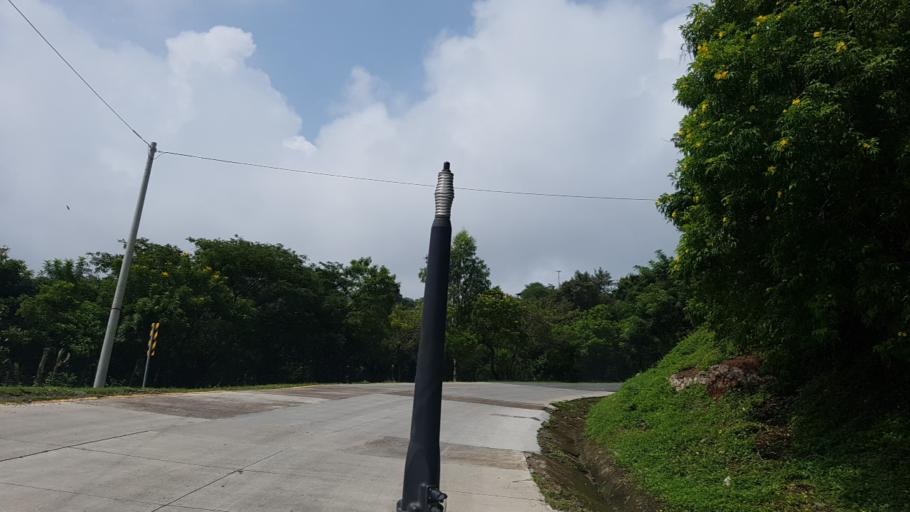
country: NI
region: Leon
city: Santa Rosa del Penon
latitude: 12.9367
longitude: -86.3398
